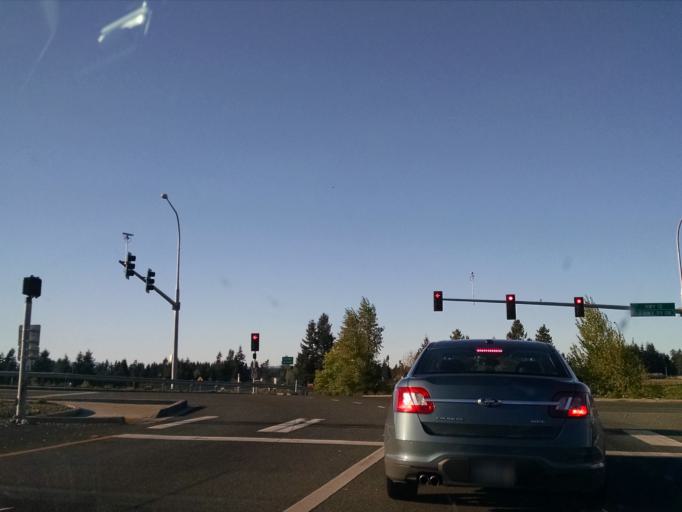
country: US
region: Washington
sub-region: Thurston County
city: Grand Mound
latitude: 46.8026
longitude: -123.0052
